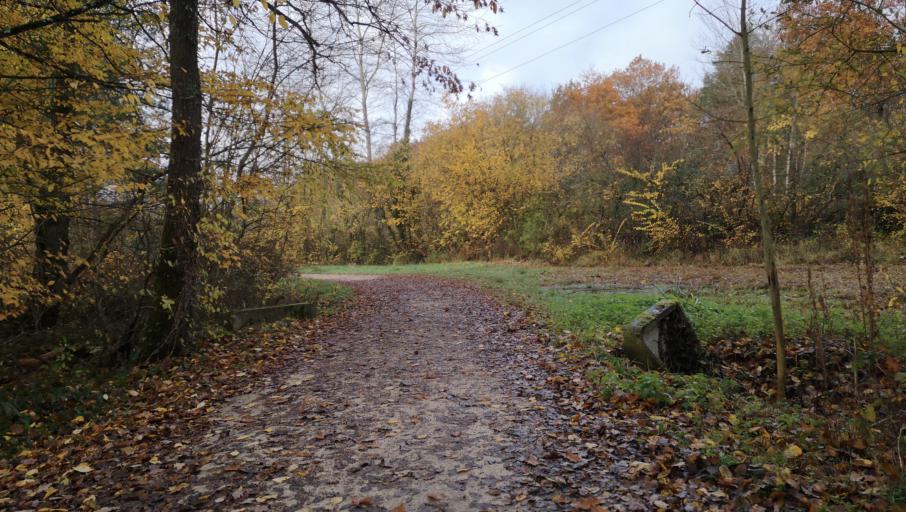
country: FR
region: Centre
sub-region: Departement du Loiret
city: Semoy
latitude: 47.9423
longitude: 1.9641
